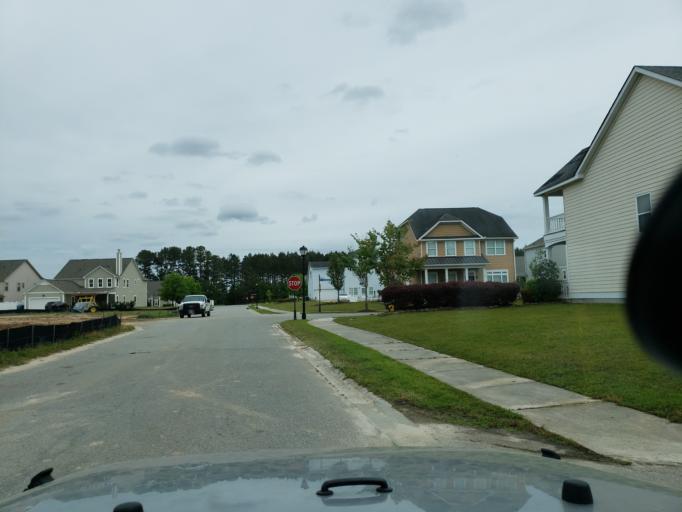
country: US
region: Georgia
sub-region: Chatham County
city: Port Wentworth
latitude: 32.2140
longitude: -81.1828
